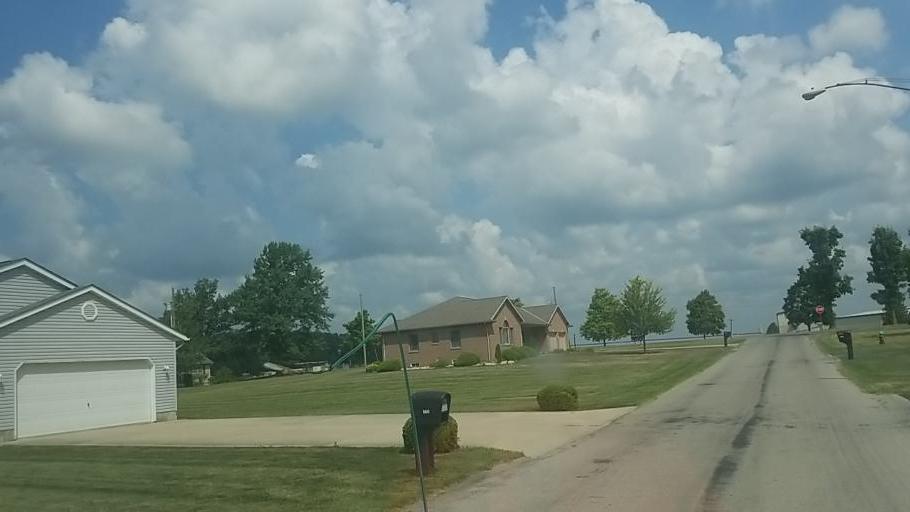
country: US
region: Ohio
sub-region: Wyandot County
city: Upper Sandusky
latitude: 40.8391
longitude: -83.2865
